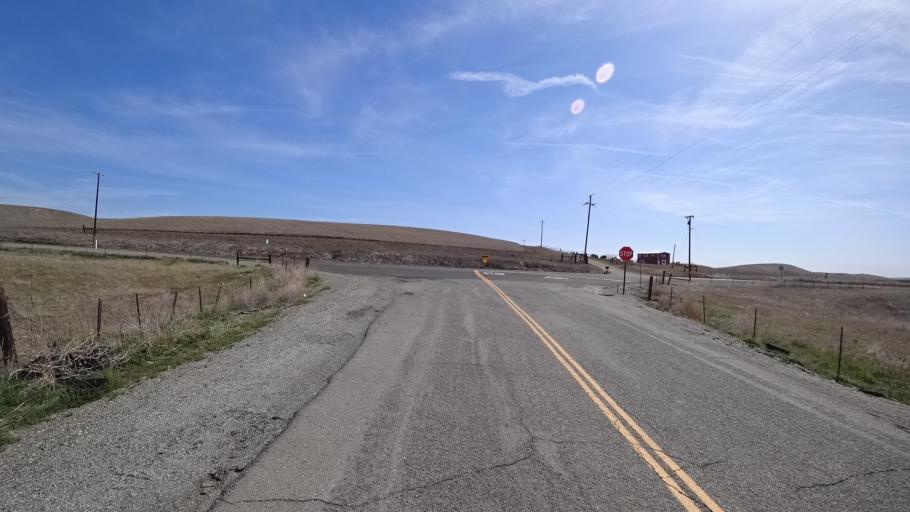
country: US
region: California
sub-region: Glenn County
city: Willows
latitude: 39.5533
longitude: -122.3581
